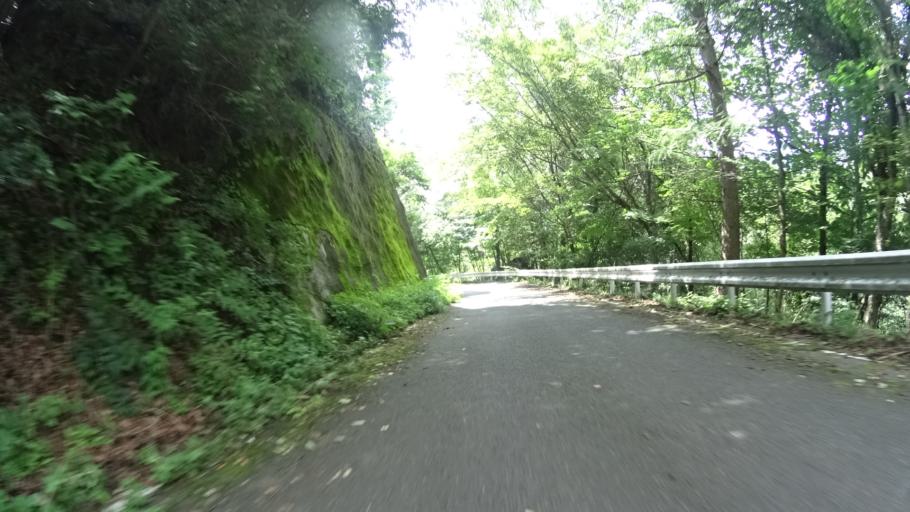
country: JP
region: Yamanashi
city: Nirasaki
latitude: 35.8816
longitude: 138.4956
